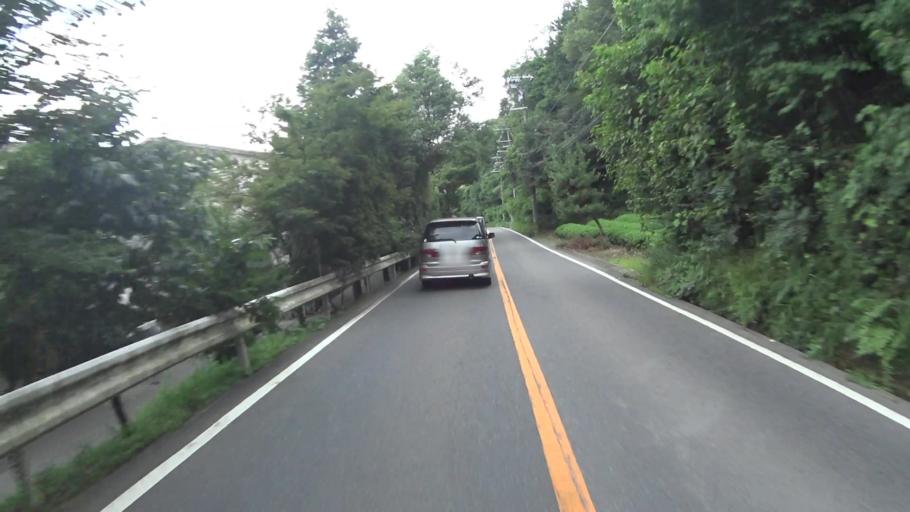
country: JP
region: Kyoto
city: Uji
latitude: 34.8599
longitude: 135.9017
